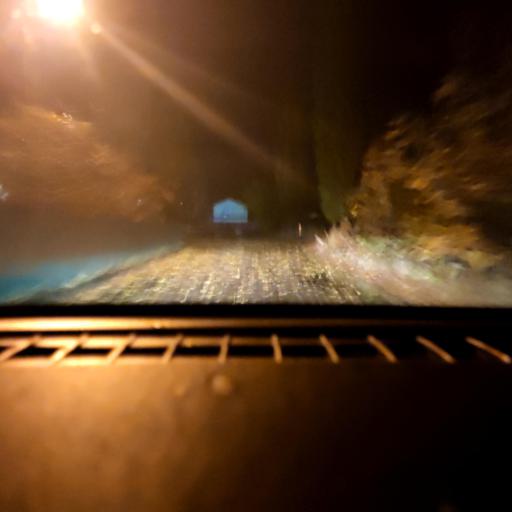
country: RU
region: Voronezj
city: Somovo
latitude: 51.7366
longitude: 39.3663
